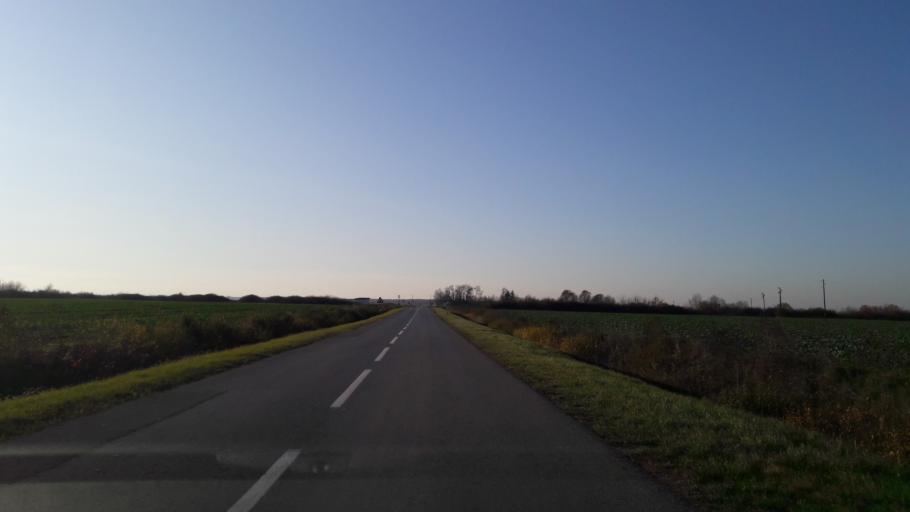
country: HR
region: Osjecko-Baranjska
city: Vuka
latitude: 45.4215
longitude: 18.5285
